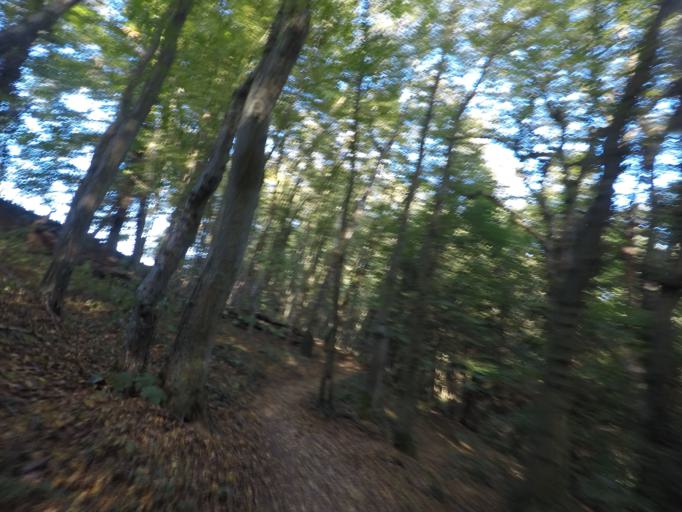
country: LU
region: Luxembourg
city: Kirchberg
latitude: 49.6040
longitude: 6.1556
